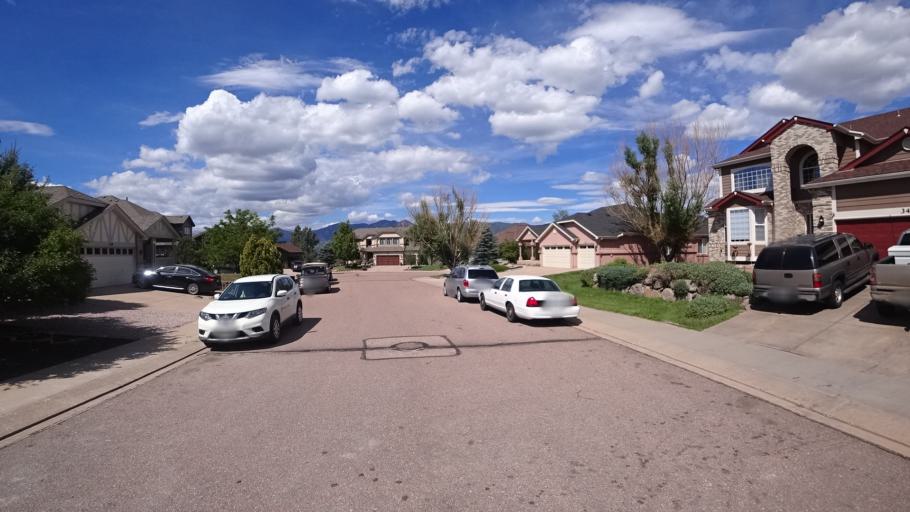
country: US
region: Colorado
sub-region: El Paso County
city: Gleneagle
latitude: 39.0292
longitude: -104.8214
